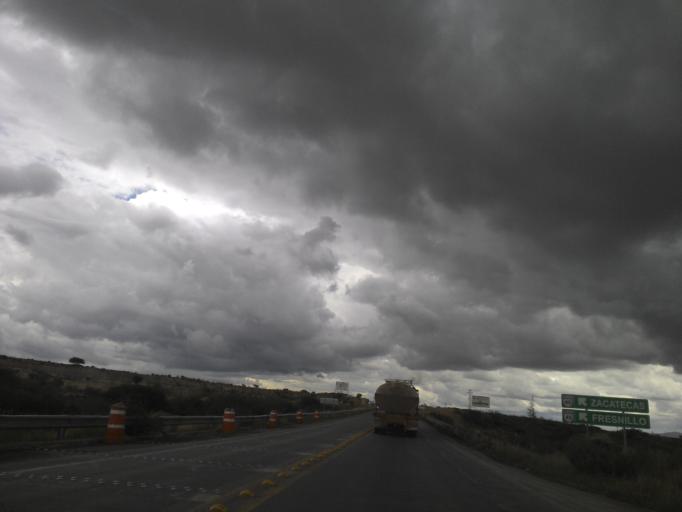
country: MX
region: Zacatecas
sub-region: Rio Grande
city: Los Condes
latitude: 23.8704
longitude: -103.0842
